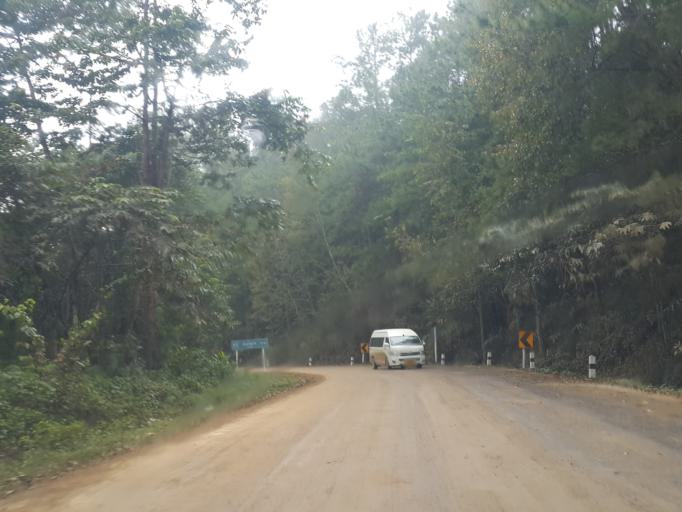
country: TH
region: Mae Hong Son
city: Mae Hi
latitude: 19.2715
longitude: 98.5786
